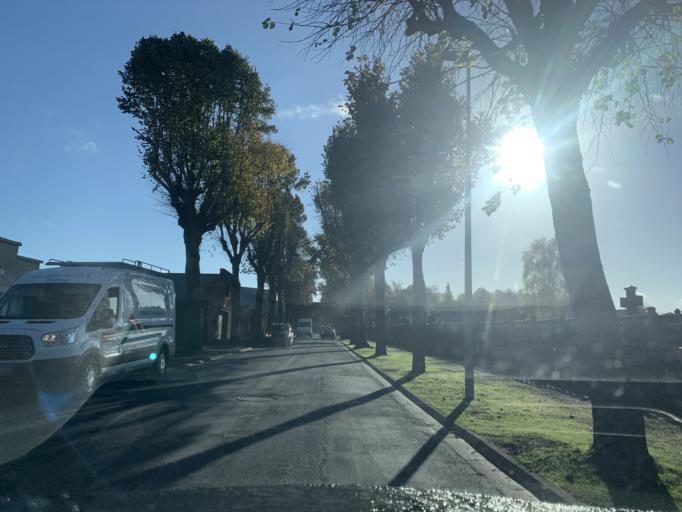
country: FR
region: Nord-Pas-de-Calais
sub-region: Departement du Nord
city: Cambrai
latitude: 50.1696
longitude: 3.2268
